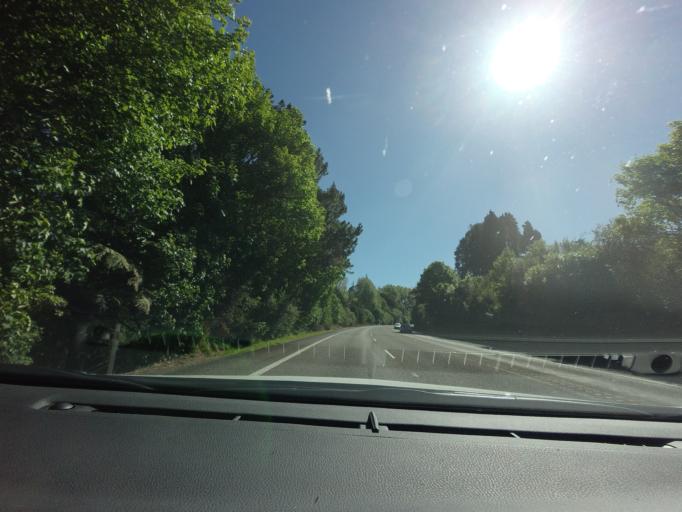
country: NZ
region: Bay of Plenty
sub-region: Rotorua District
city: Rotorua
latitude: -38.0756
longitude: 176.1630
